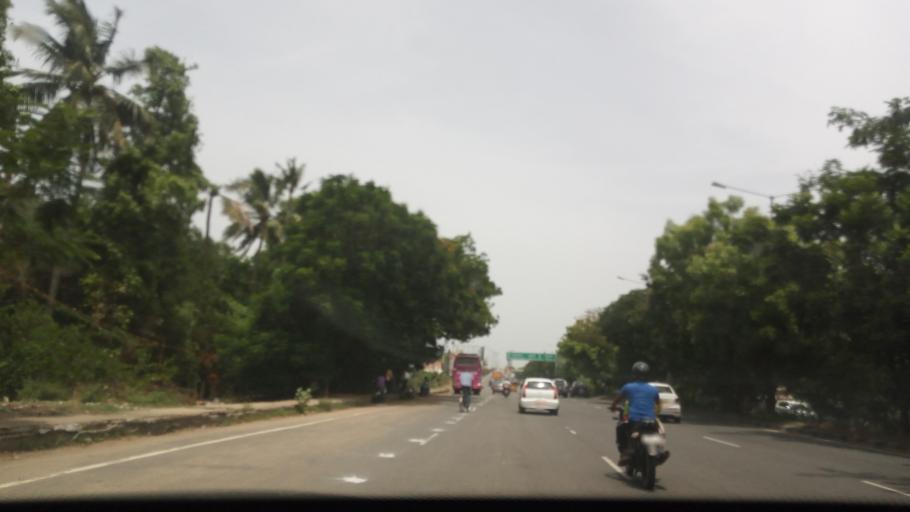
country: IN
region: Tamil Nadu
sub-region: Kancheepuram
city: Vandalur
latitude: 12.8963
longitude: 80.0888
